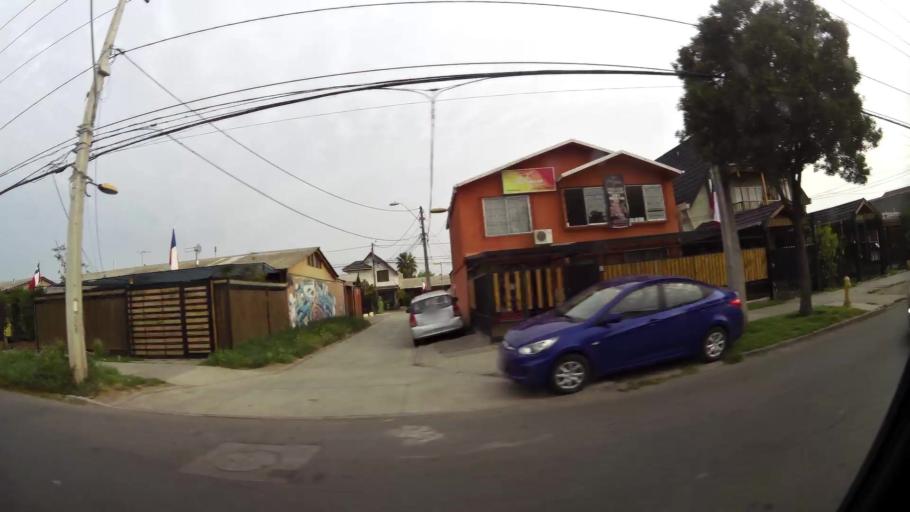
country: CL
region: Santiago Metropolitan
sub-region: Provincia de Santiago
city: Lo Prado
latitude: -33.5218
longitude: -70.7809
